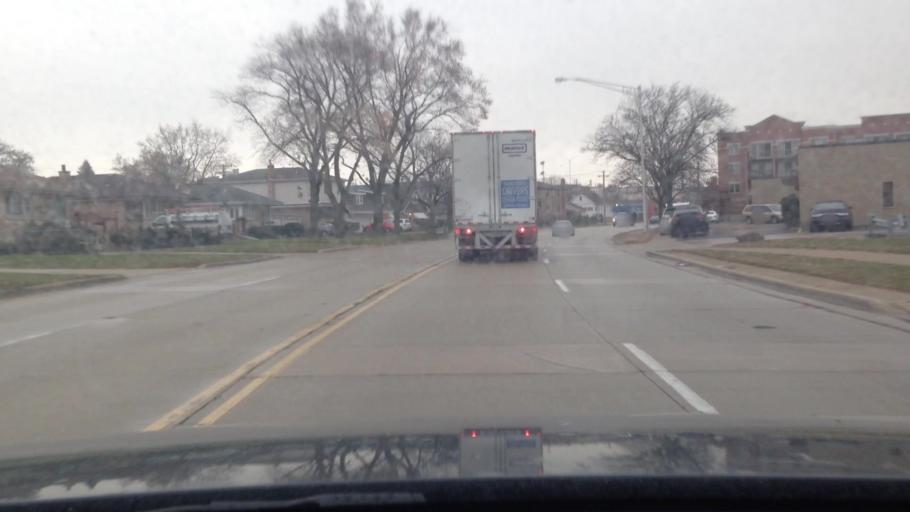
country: US
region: Illinois
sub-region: Cook County
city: Schiller Park
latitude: 41.9626
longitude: -87.8731
